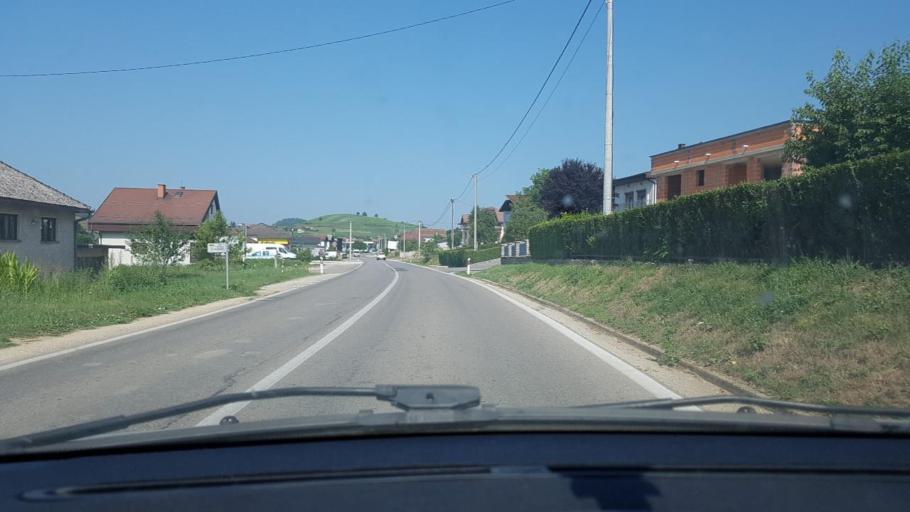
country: BA
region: Federation of Bosnia and Herzegovina
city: Mala Kladusa
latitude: 45.1323
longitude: 15.8604
